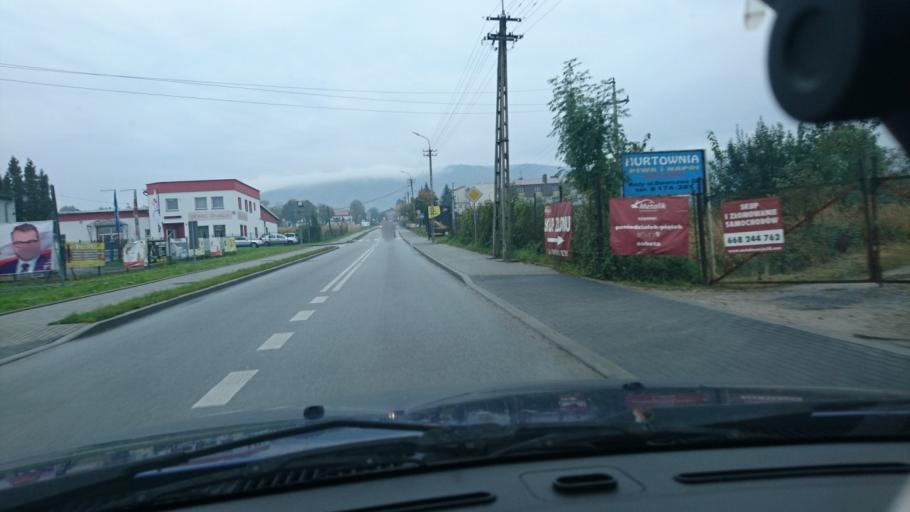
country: PL
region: Silesian Voivodeship
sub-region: Powiat bielski
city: Kozy
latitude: 49.8498
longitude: 19.1445
